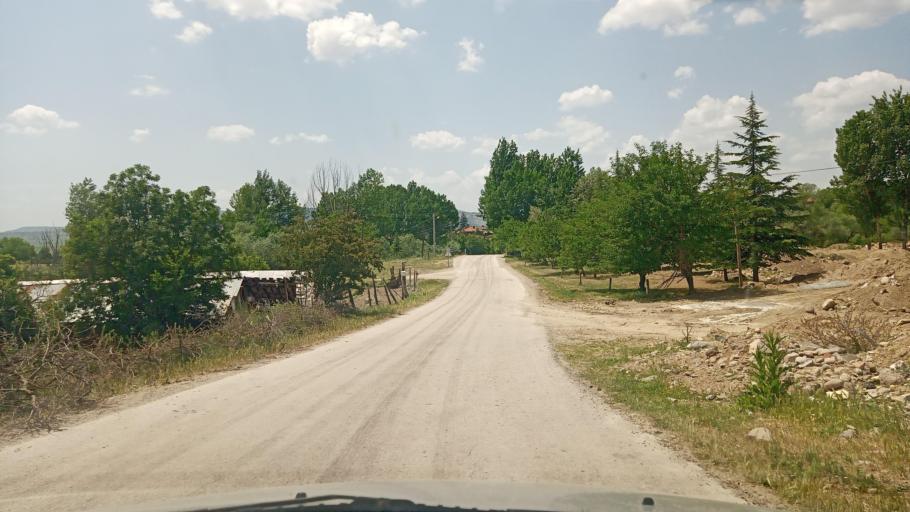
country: TR
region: Bolu
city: Seben
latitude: 40.4071
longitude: 31.5812
